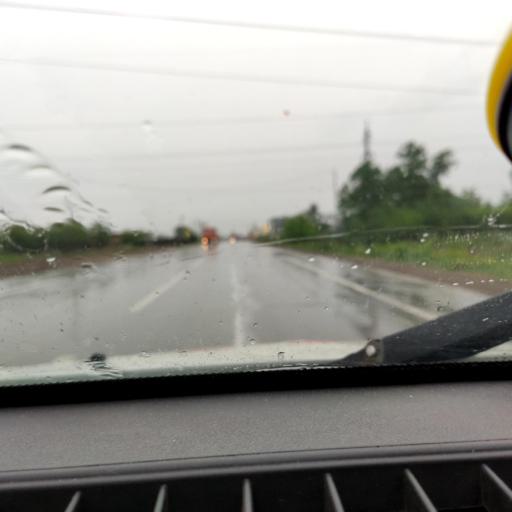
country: RU
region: Samara
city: Tol'yatti
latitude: 53.5815
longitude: 49.4037
